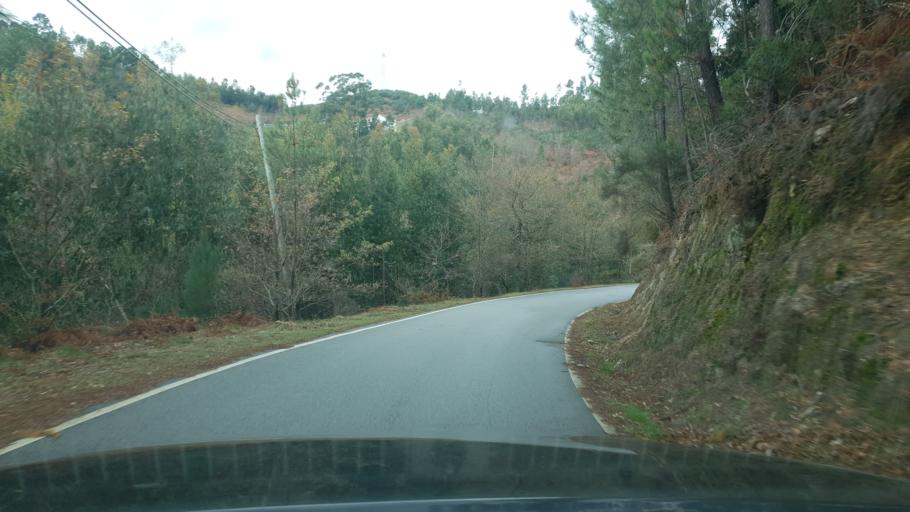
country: PT
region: Viseu
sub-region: Castro Daire
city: Castro Daire
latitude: 40.8844
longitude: -8.0138
